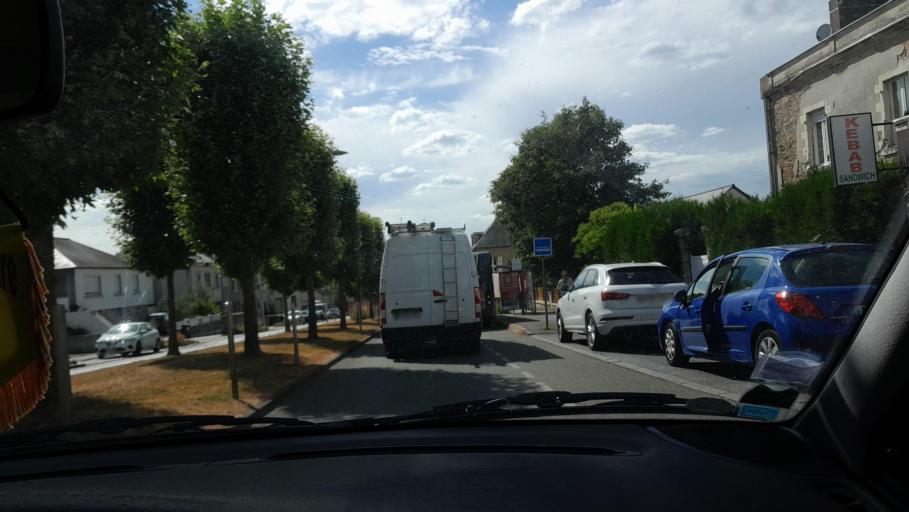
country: FR
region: Pays de la Loire
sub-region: Departement de la Mayenne
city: Saint-Berthevin
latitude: 48.0699
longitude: -0.8327
